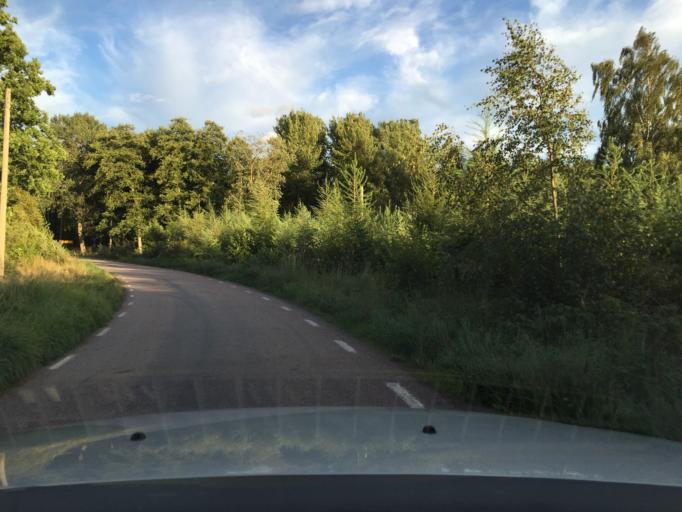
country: SE
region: Skane
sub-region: Hassleholms Kommun
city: Tormestorp
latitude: 56.0163
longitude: 13.7751
